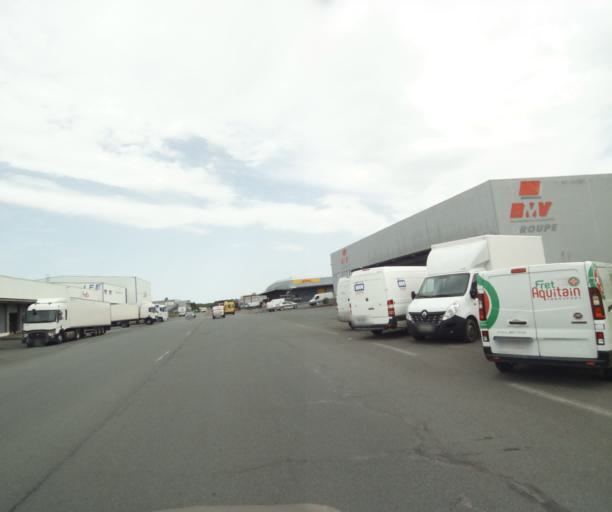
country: FR
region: Aquitaine
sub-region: Departement des Pyrenees-Atlantiques
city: Mouguerre
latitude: 43.4880
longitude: -1.4292
